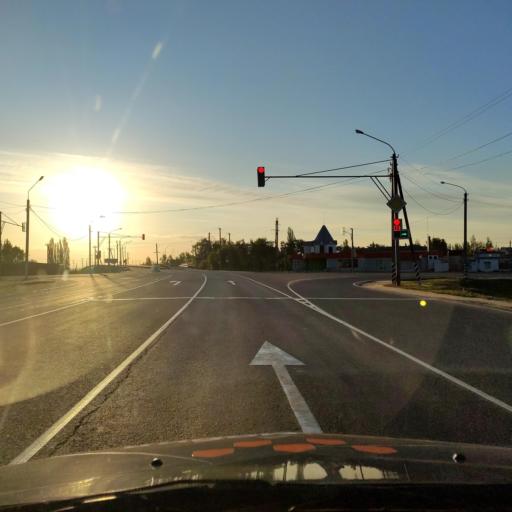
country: RU
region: Orjol
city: Livny
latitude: 52.4412
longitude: 37.5755
